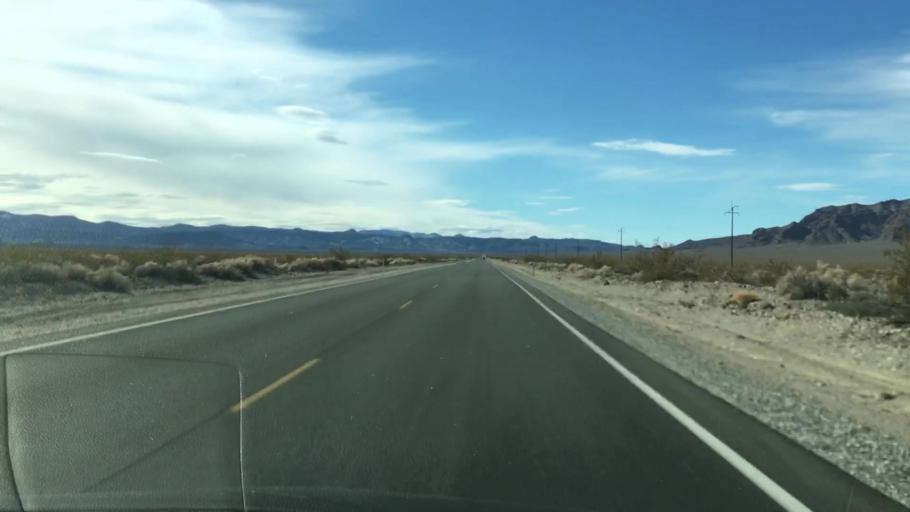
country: US
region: Nevada
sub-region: Nye County
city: Pahrump
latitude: 36.3042
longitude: -116.4382
